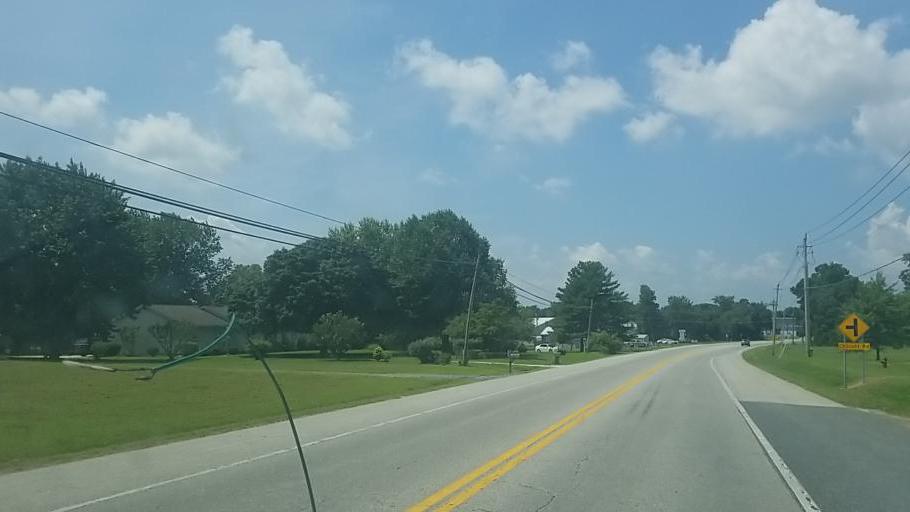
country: US
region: Maryland
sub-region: Talbot County
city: Easton
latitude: 38.7711
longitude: -76.0491
